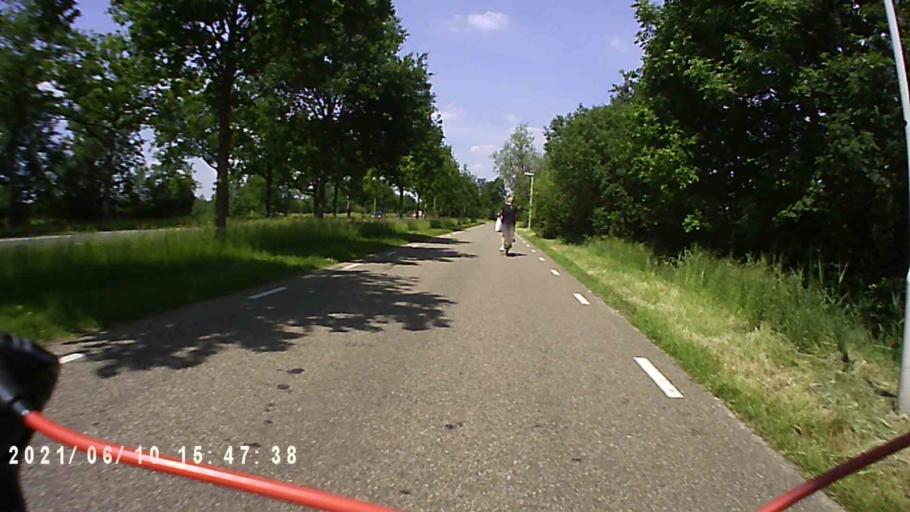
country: NL
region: Friesland
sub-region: Gemeente Smallingerland
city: Rottevalle
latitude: 53.1617
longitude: 6.1181
